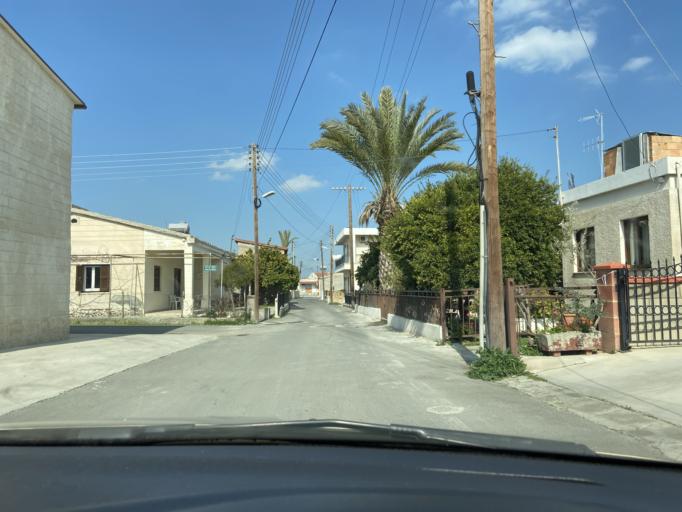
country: CY
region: Lefkosia
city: Alampra
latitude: 35.0121
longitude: 33.3889
